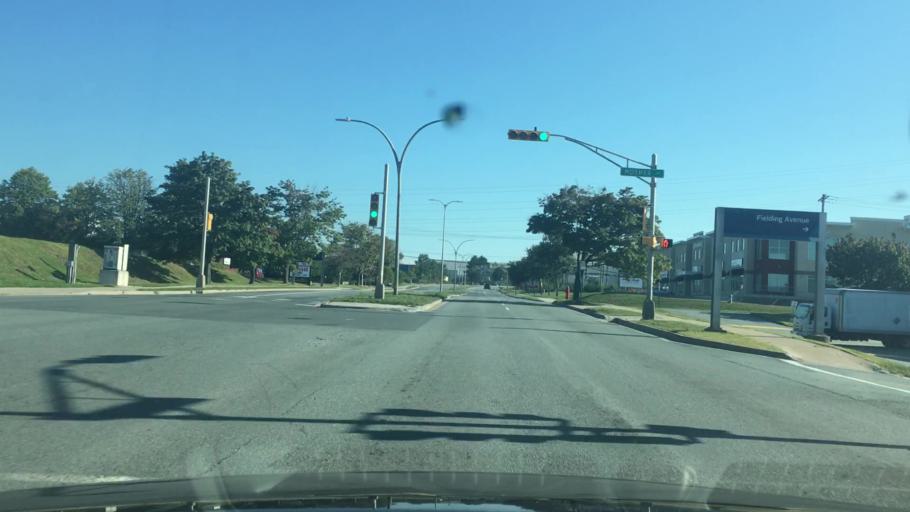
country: CA
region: Nova Scotia
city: Dartmouth
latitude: 44.7075
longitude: -63.6078
